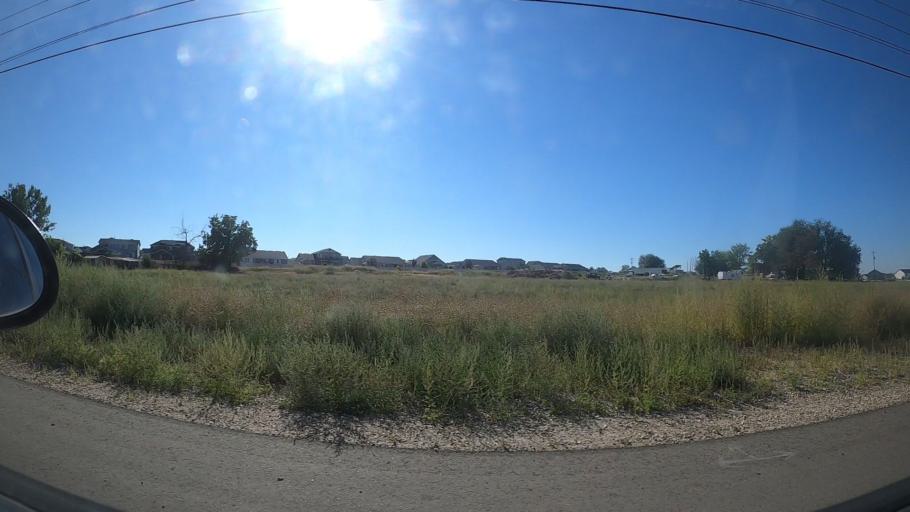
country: US
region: Idaho
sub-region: Canyon County
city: Nampa
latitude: 43.5617
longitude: -116.6129
